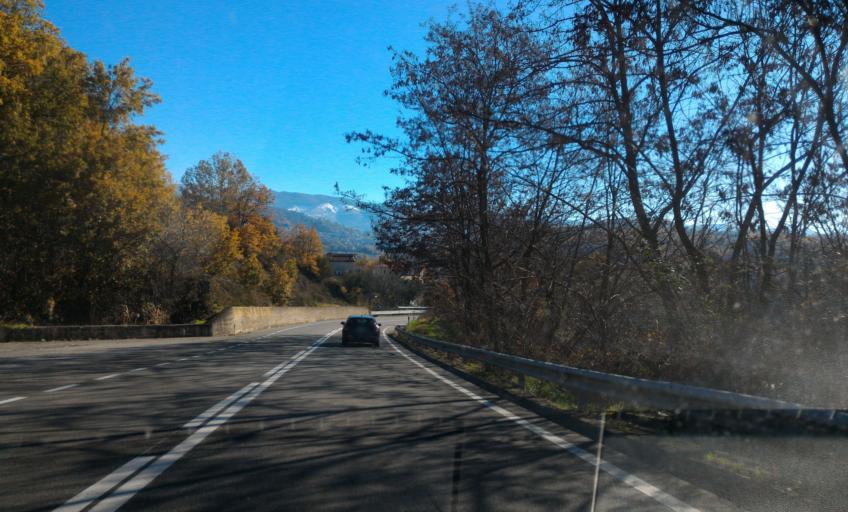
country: IT
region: Calabria
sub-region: Provincia di Cosenza
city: Rovito
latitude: 39.3028
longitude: 16.3123
